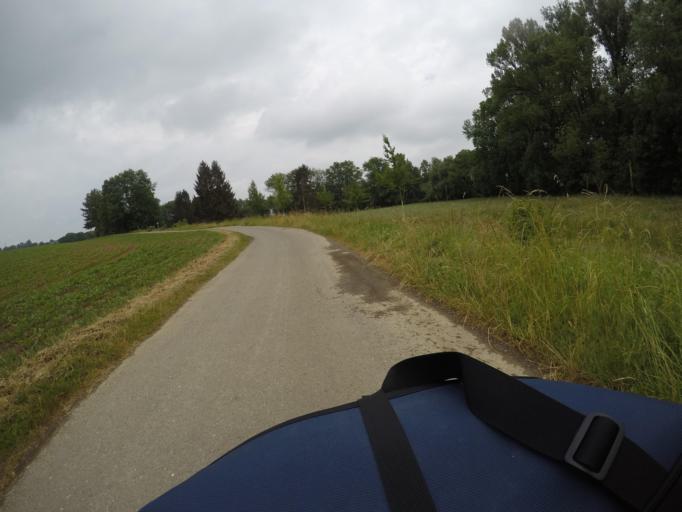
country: DE
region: Baden-Wuerttemberg
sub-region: Regierungsbezirk Stuttgart
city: Ditzingen
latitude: 48.8377
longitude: 9.0584
